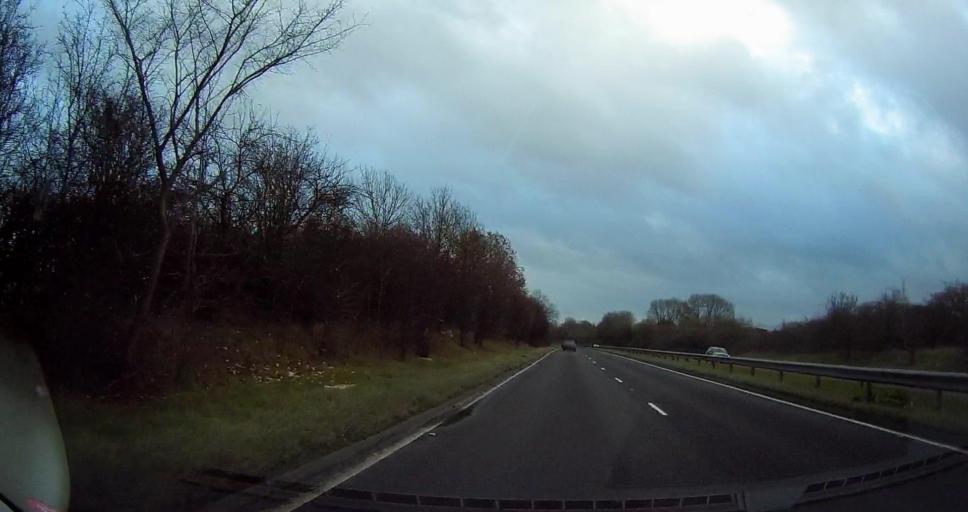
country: GB
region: England
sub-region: Derbyshire
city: Chesterfield
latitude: 53.2169
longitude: -1.3952
